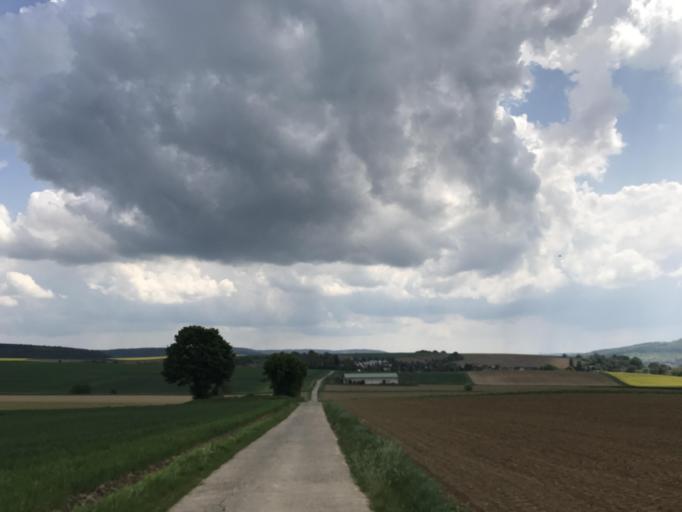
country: DE
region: Hesse
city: Ortenberg
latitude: 50.3224
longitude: 9.0575
